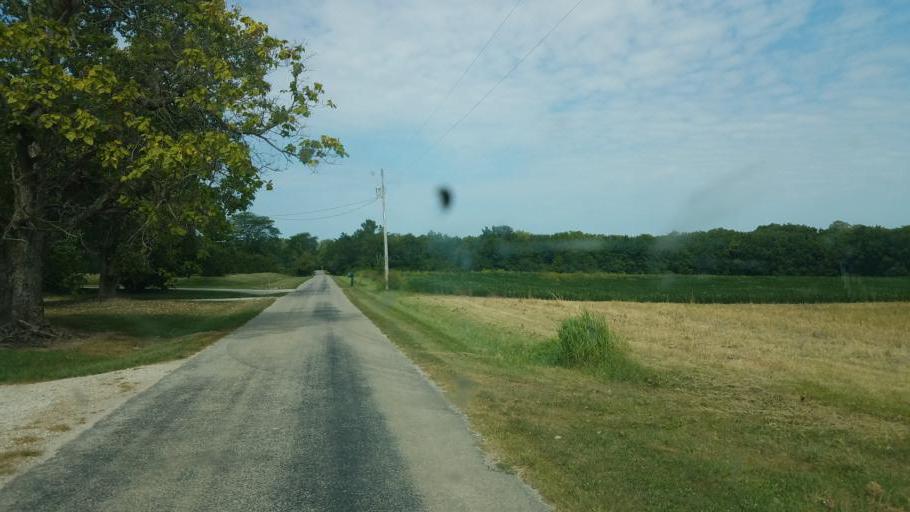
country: US
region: Ohio
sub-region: Delaware County
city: Ashley
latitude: 40.4465
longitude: -83.0369
